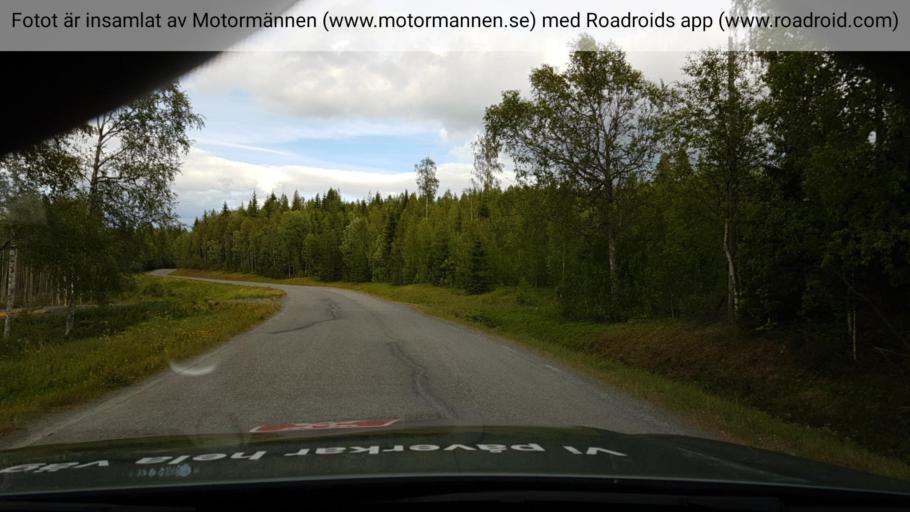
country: SE
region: Jaemtland
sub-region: OEstersunds Kommun
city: Lit
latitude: 63.3080
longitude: 14.8867
